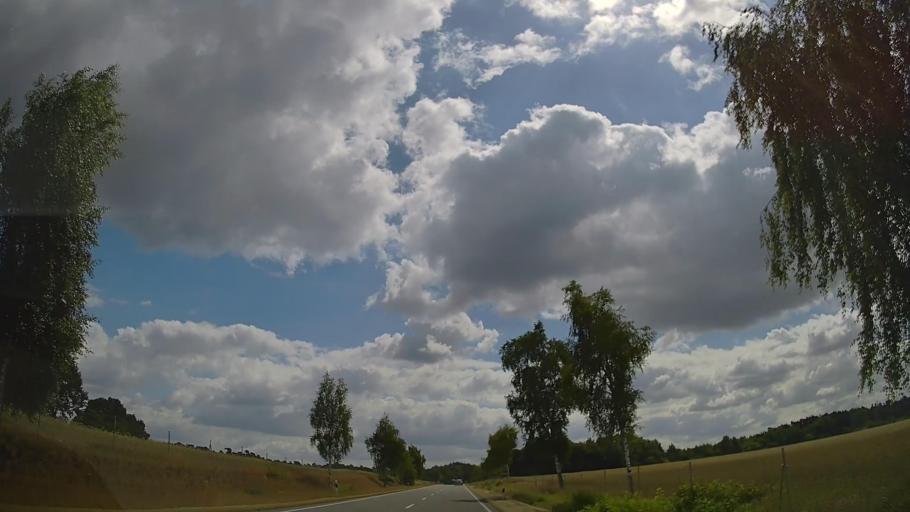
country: DE
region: Lower Saxony
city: Vechta
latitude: 52.7029
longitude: 8.2898
